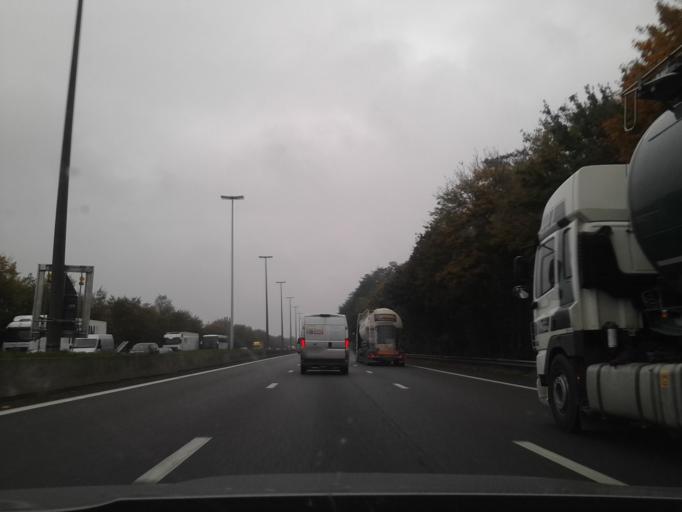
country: BE
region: Wallonia
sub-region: Province du Hainaut
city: Quaregnon
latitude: 50.4533
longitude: 3.8685
